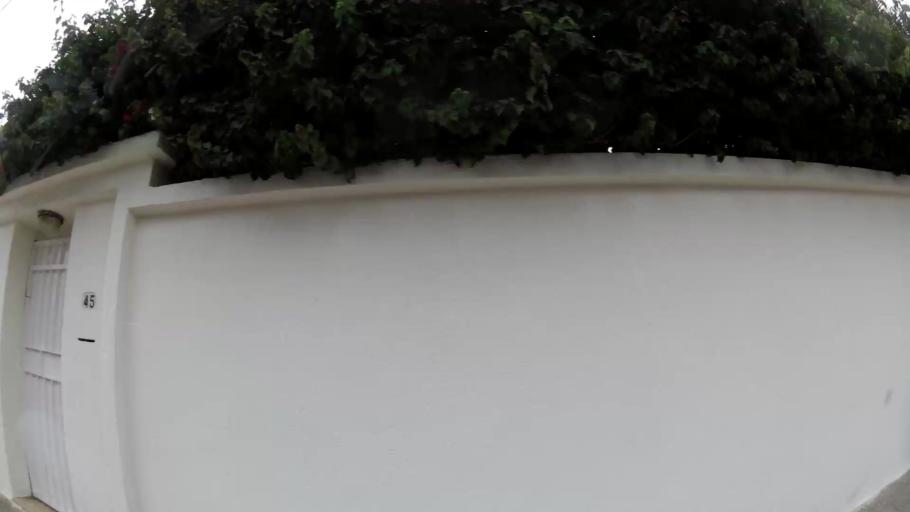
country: MA
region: Rabat-Sale-Zemmour-Zaer
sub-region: Rabat
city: Rabat
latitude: 33.9859
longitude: -6.8271
